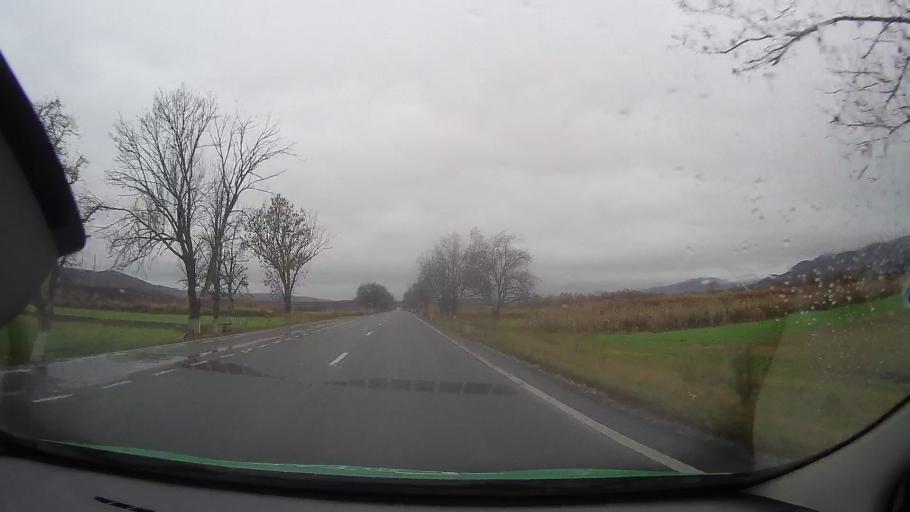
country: RO
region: Mures
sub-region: Comuna Suseni
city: Suseni
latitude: 46.8314
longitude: 24.7419
